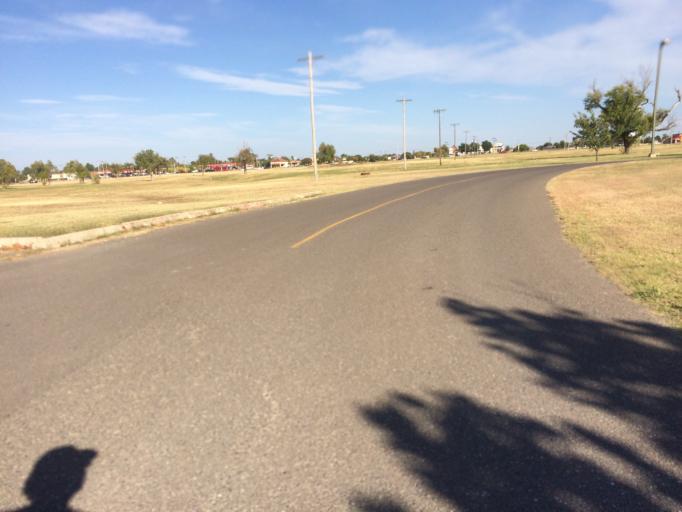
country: US
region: Oklahoma
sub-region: Cleveland County
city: Norman
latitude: 35.2304
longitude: -97.4284
